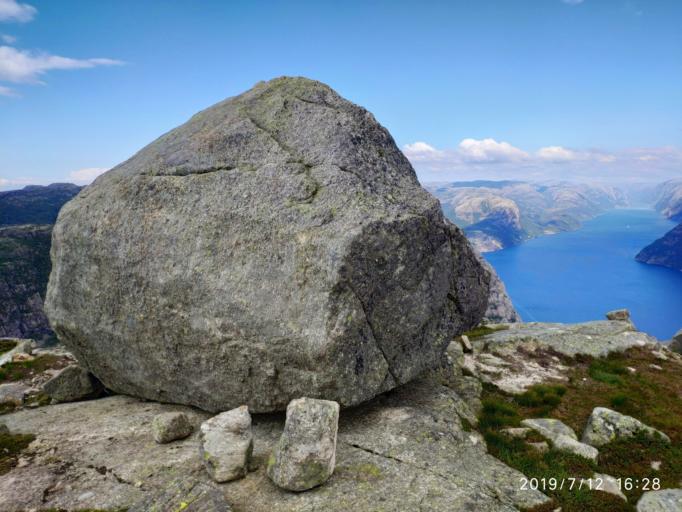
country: NO
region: Rogaland
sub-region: Forsand
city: Forsand
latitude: 58.9853
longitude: 6.1843
